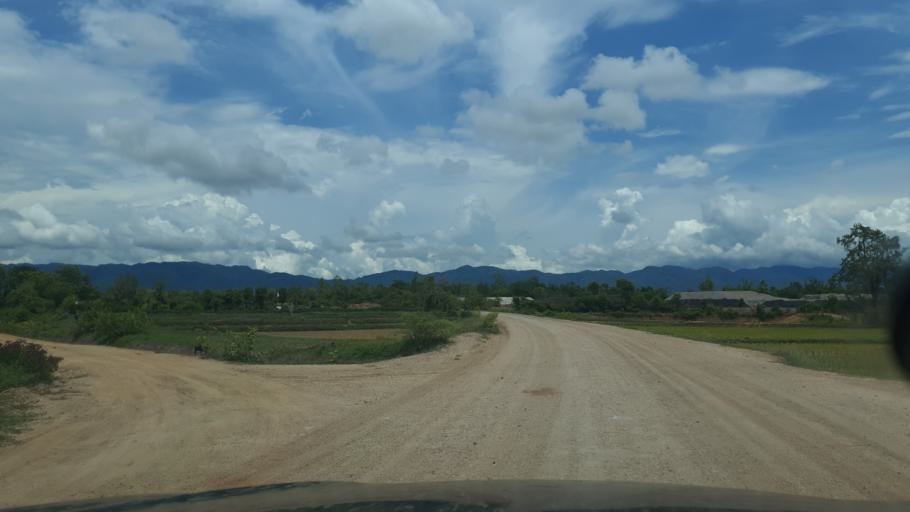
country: TH
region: Lampang
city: Sop Prap
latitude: 17.9368
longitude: 99.3626
